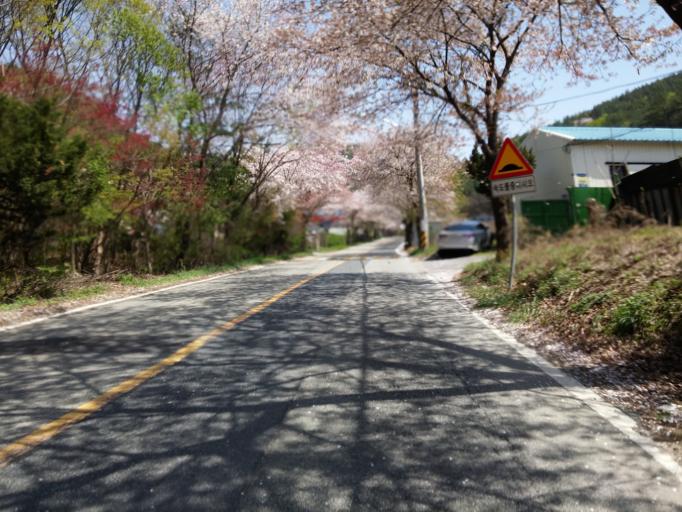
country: KR
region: Daejeon
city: Daejeon
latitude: 36.2815
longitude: 127.4773
